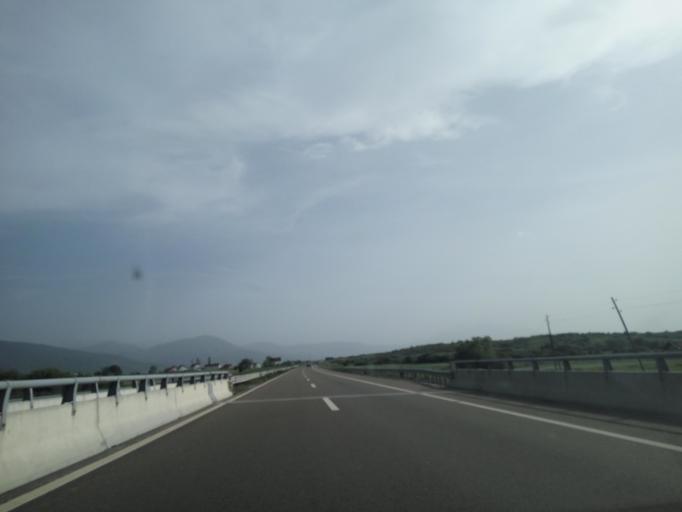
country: XK
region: Prizren
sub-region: Komuna e Therandes
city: Leshan
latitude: 42.2994
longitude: 20.7628
